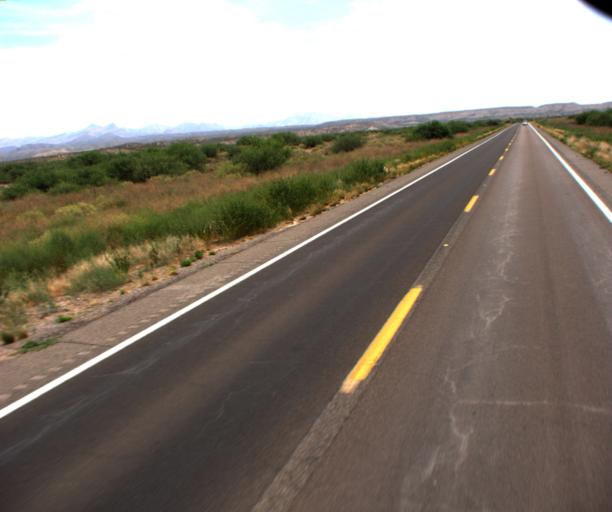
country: US
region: Arizona
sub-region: Graham County
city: Bylas
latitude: 33.1776
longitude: -110.1466
